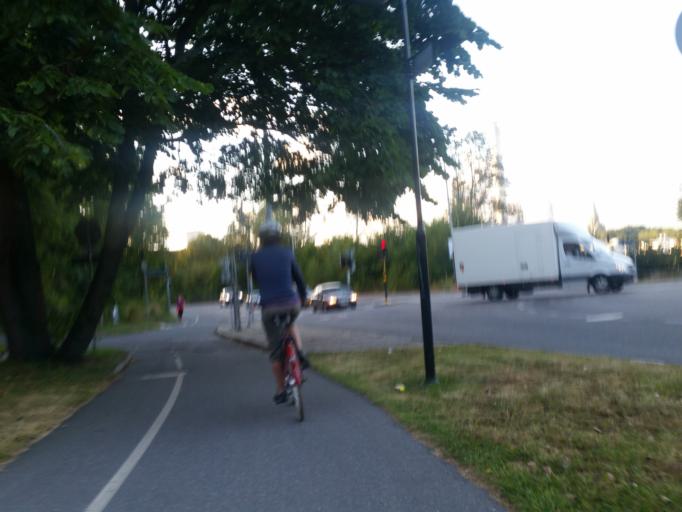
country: SE
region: Stockholm
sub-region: Stockholms Kommun
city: Arsta
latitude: 59.2994
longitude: 18.0858
